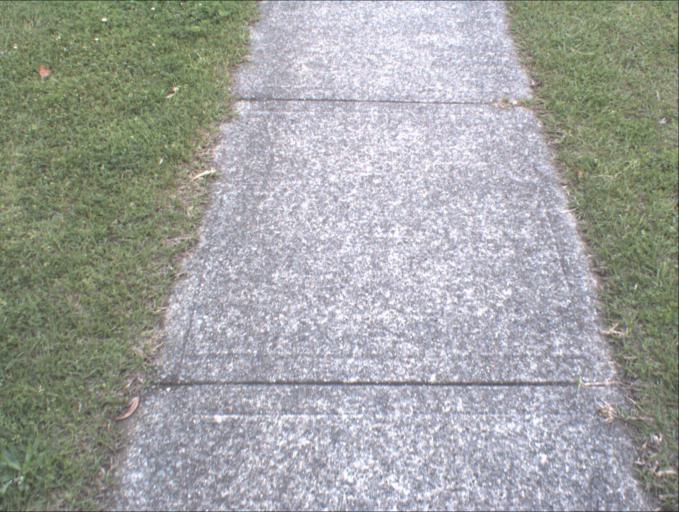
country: AU
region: Queensland
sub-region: Logan
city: Waterford West
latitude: -27.6948
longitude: 153.1540
